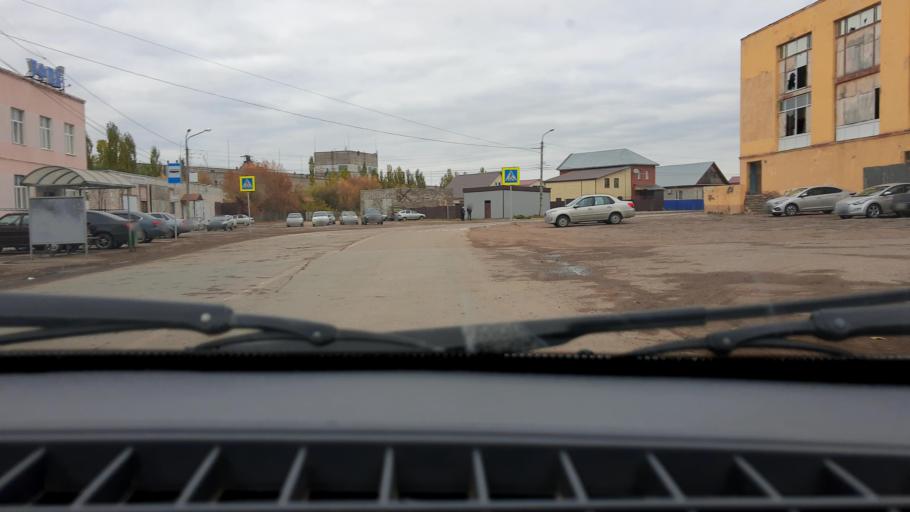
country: RU
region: Bashkortostan
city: Mikhaylovka
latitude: 54.7452
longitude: 55.8996
